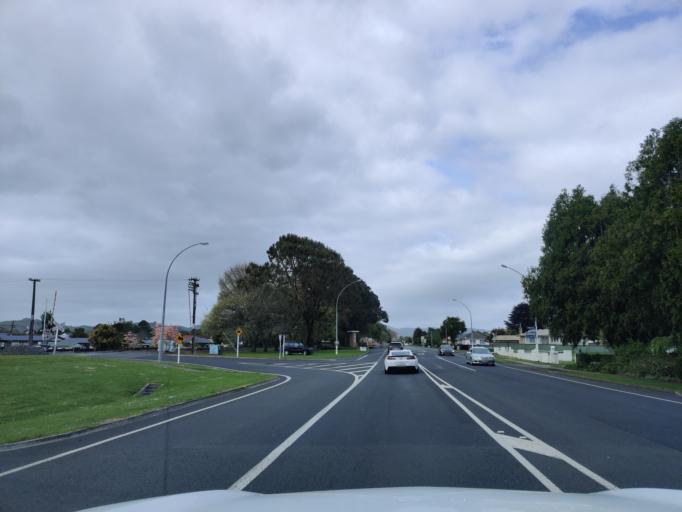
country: NZ
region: Waikato
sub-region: Waikato District
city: Ngaruawahia
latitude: -37.5385
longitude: 175.1585
